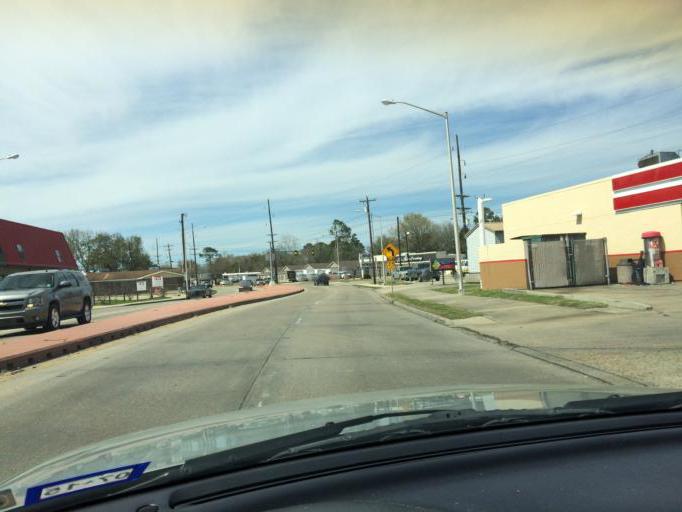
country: US
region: Louisiana
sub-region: Lafayette Parish
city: Lafayette
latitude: 30.1939
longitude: -92.0588
